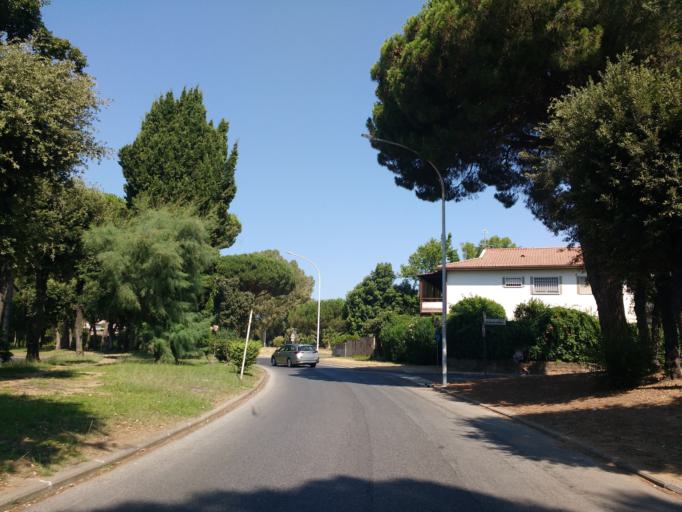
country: IT
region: Latium
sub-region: Citta metropolitana di Roma Capitale
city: Acilia-Castel Fusano-Ostia Antica
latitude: 41.7582
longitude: 12.3601
